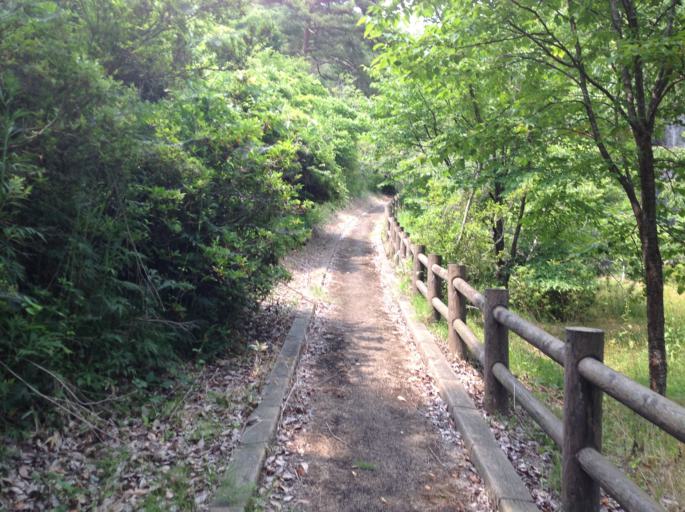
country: JP
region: Iwate
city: Ichinoseki
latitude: 38.8539
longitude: 141.2338
